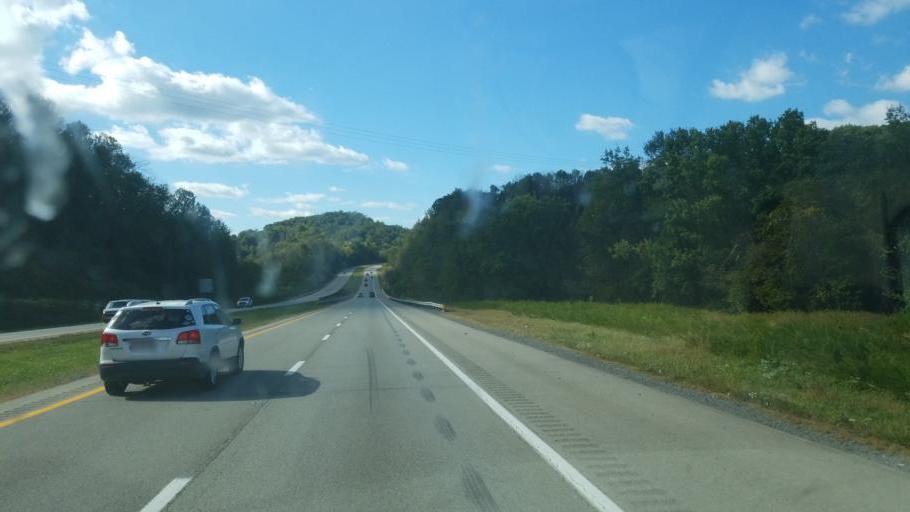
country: US
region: West Virginia
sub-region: Monongalia County
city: Star City
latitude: 39.6658
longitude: -80.0181
